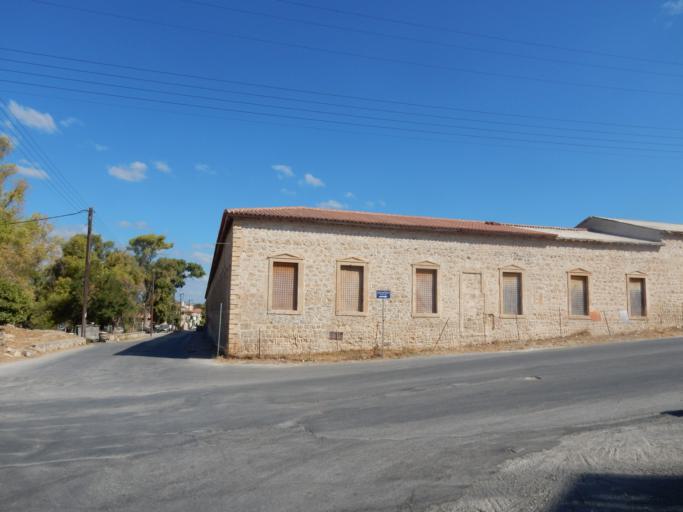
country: GR
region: Attica
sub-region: Nomos Piraios
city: Aegina
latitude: 37.7424
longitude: 23.4338
